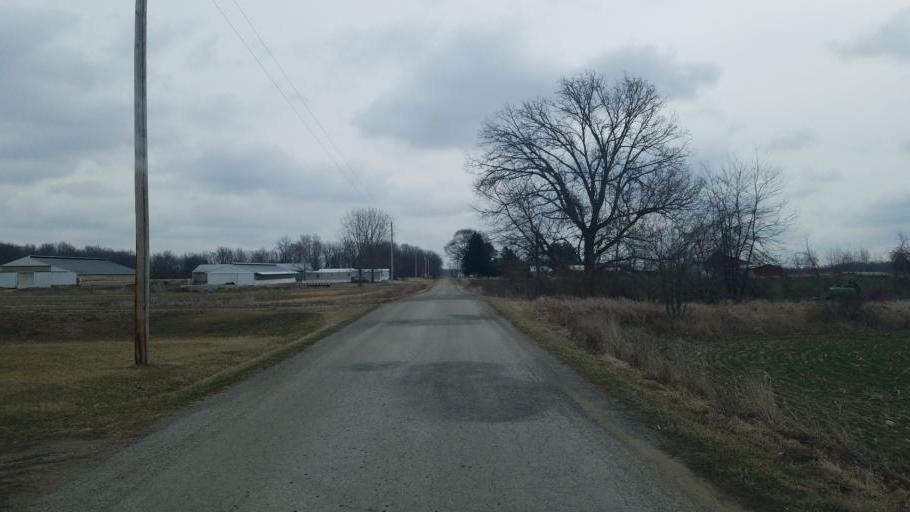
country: US
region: Ohio
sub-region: Morrow County
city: Mount Gilead
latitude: 40.6011
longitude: -82.8793
